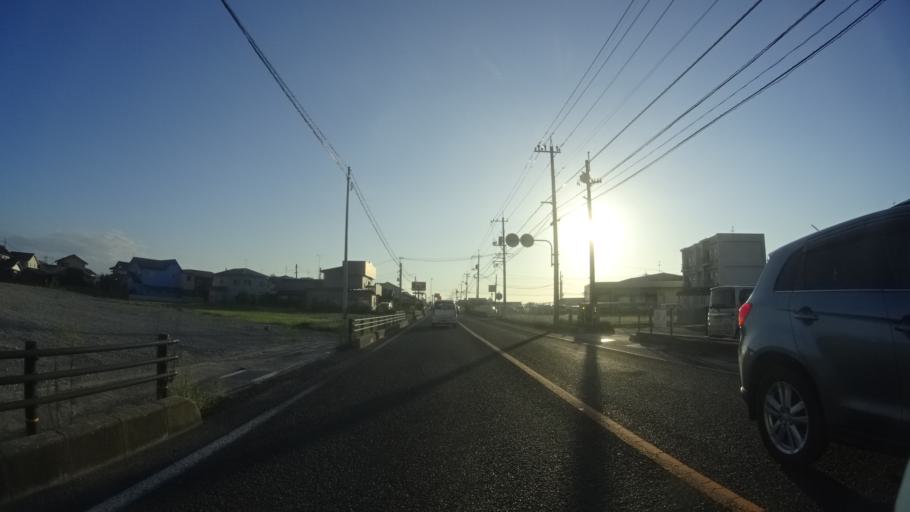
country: JP
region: Tottori
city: Yonago
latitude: 35.4501
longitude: 133.4092
